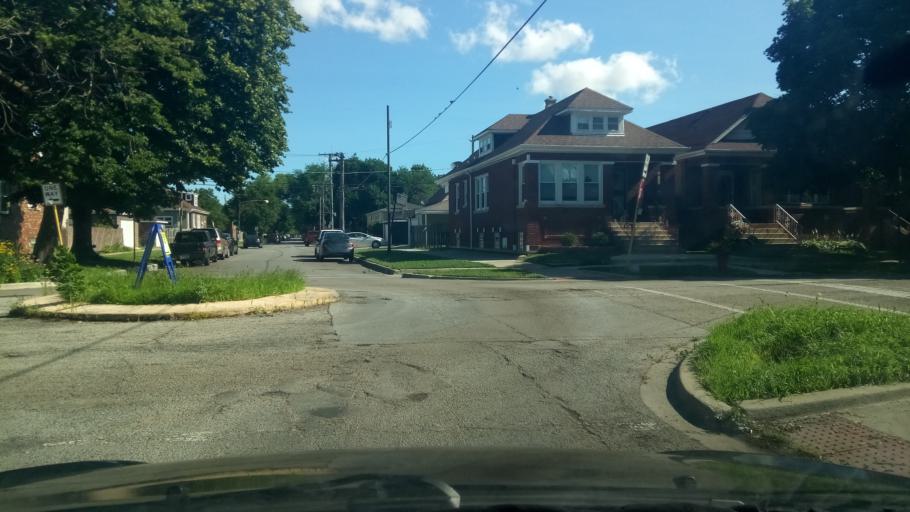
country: US
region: Illinois
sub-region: Cook County
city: Hometown
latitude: 41.7813
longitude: -87.7180
